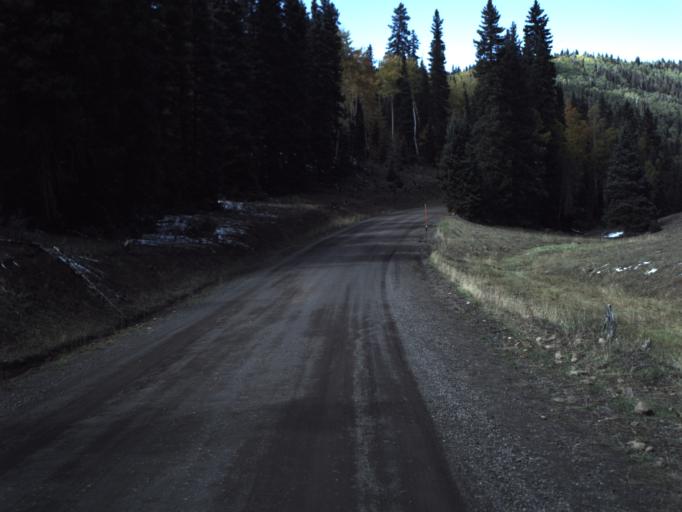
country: US
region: Utah
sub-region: Piute County
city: Junction
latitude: 38.2376
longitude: -112.3659
